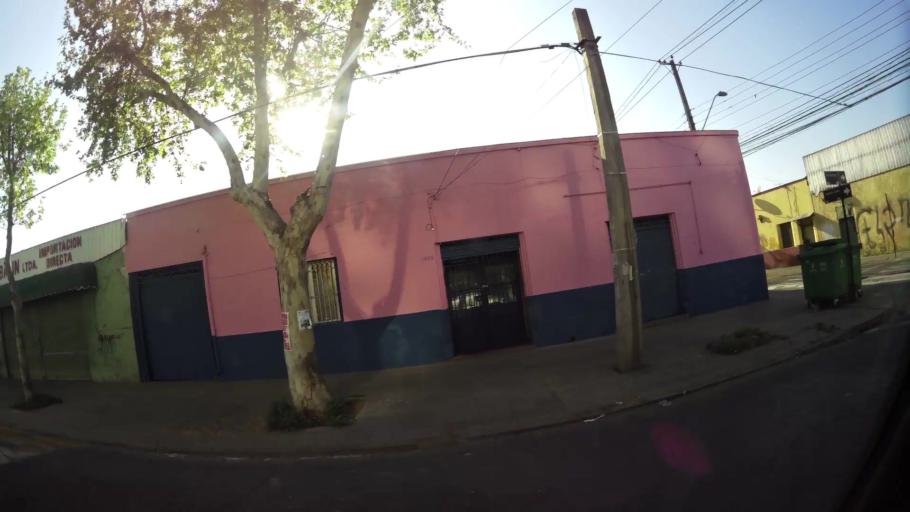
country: CL
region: Santiago Metropolitan
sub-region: Provincia de Santiago
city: Santiago
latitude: -33.4707
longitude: -70.6468
